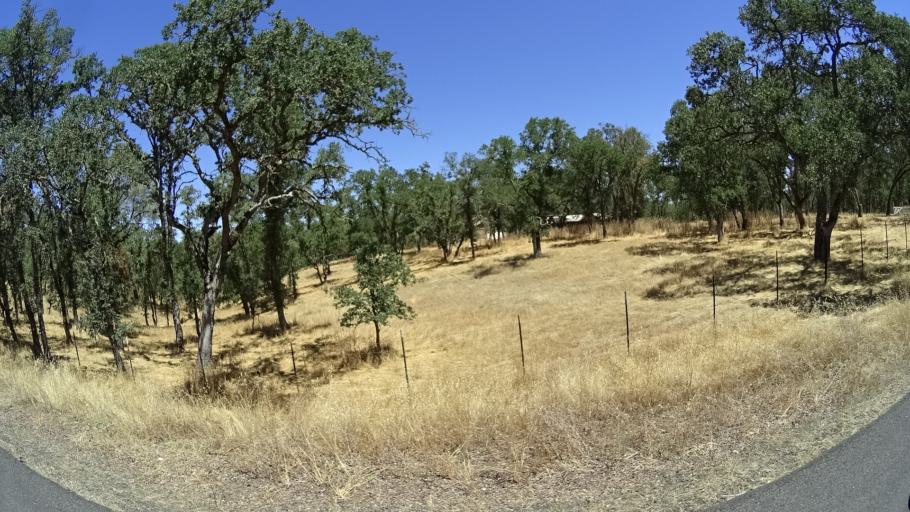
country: US
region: California
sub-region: Calaveras County
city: Copperopolis
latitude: 37.9826
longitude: -120.7005
